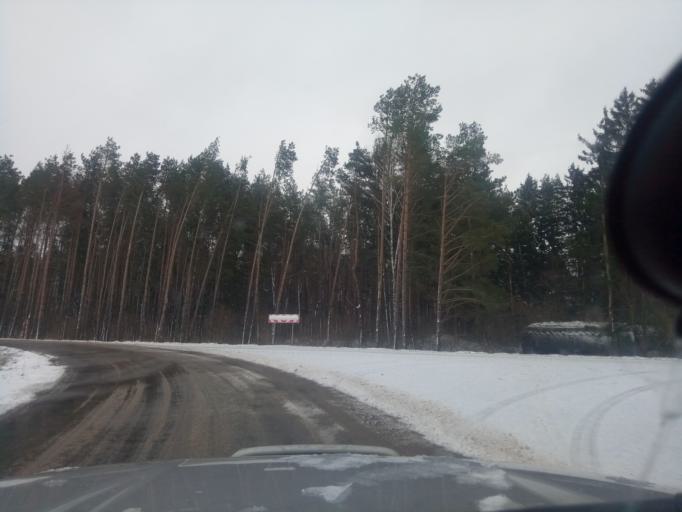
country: BY
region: Minsk
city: Tsimkavichy
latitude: 53.0425
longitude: 26.8442
